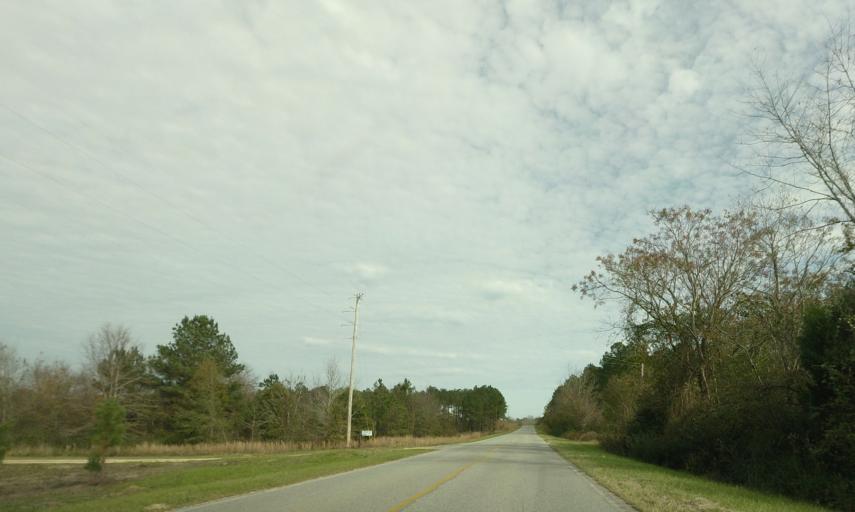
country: US
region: Georgia
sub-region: Dodge County
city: Chester
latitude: 32.4796
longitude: -83.0966
